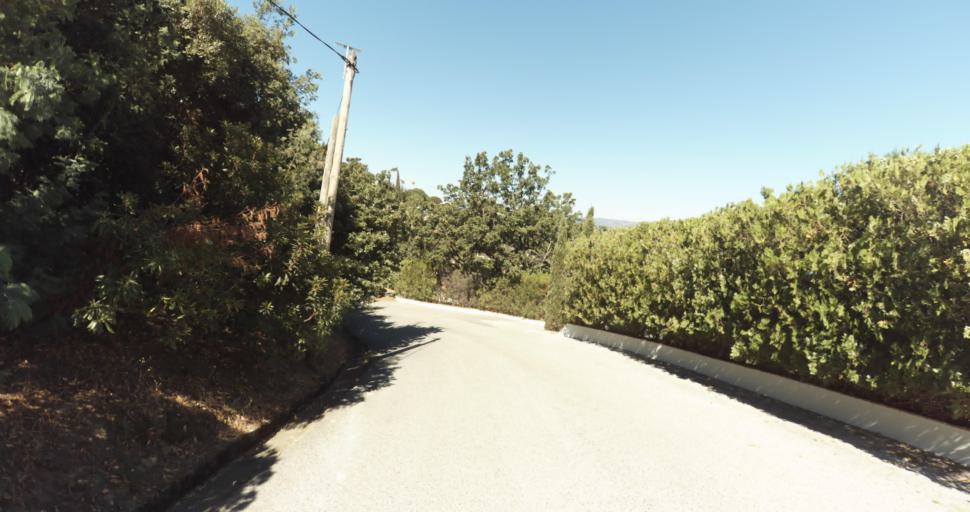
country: FR
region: Provence-Alpes-Cote d'Azur
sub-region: Departement du Var
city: Saint-Tropez
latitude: 43.2589
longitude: 6.6116
